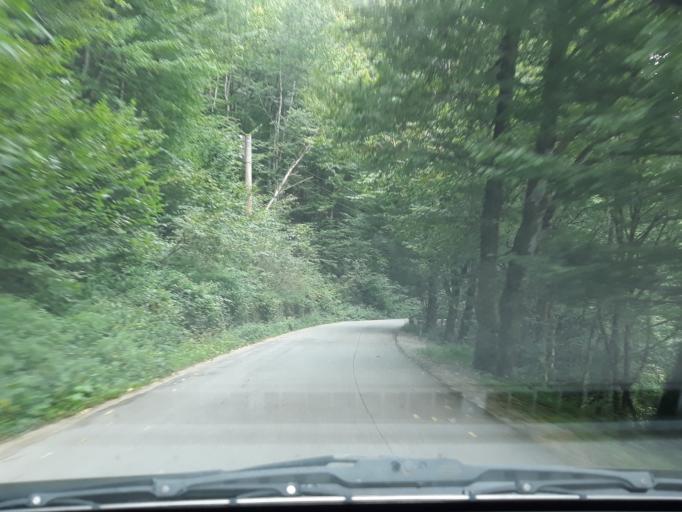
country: RO
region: Bihor
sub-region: Comuna Pietroasa
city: Pietroasa
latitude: 46.5878
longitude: 22.6213
